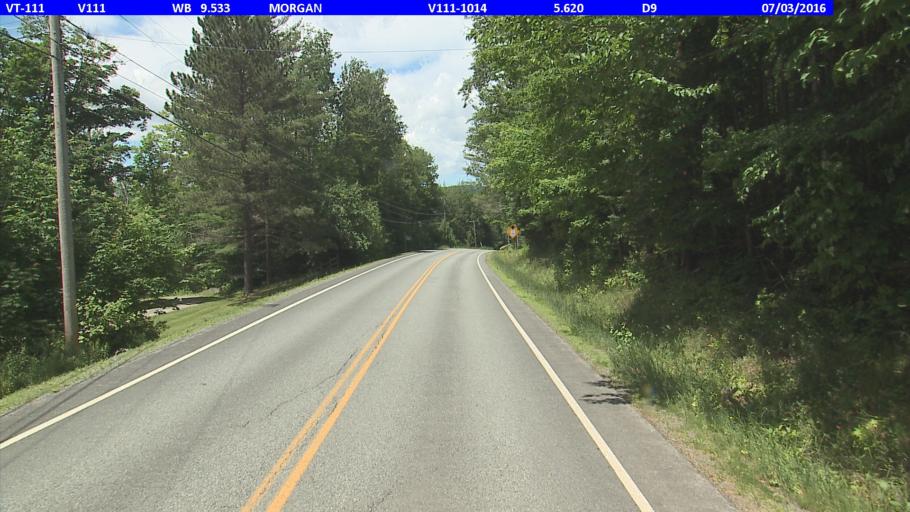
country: US
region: Vermont
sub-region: Orleans County
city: Newport
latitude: 44.9000
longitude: -71.9743
